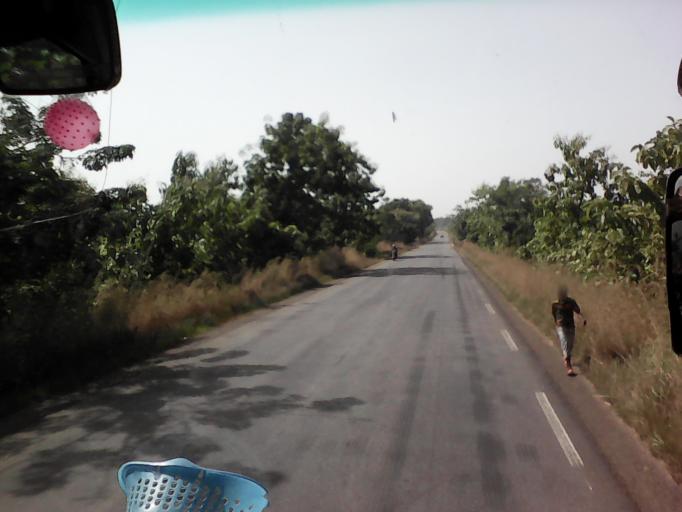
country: TG
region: Centrale
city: Sotouboua
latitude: 8.7481
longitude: 1.0561
